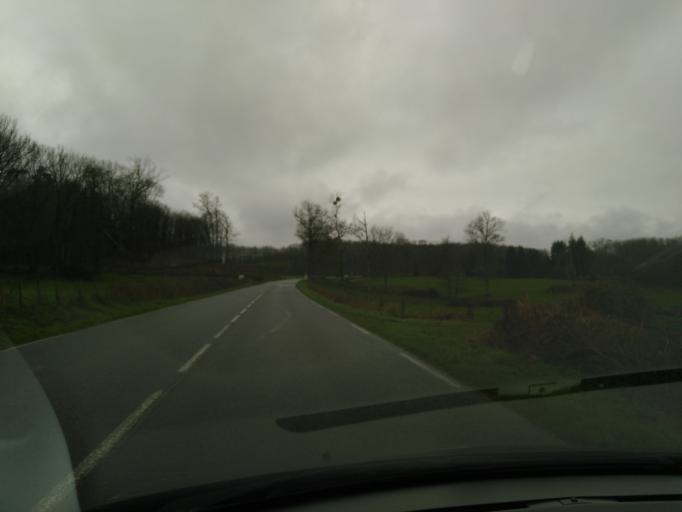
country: FR
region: Limousin
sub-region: Departement de la Haute-Vienne
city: Solignac
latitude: 45.7320
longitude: 1.2688
